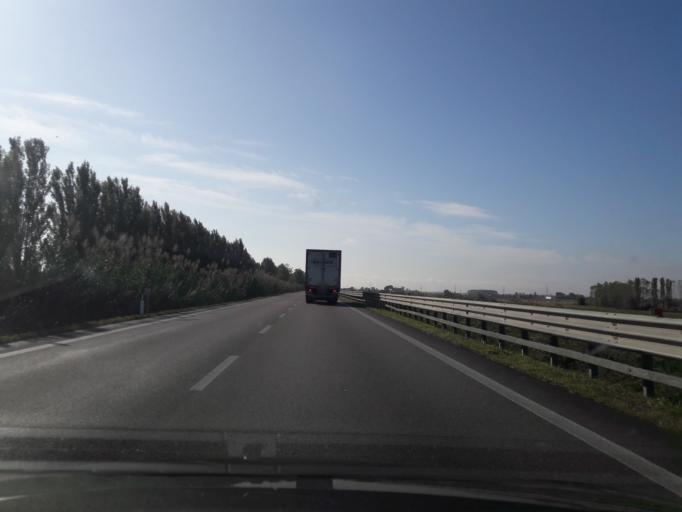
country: IT
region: Veneto
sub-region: Provincia di Padova
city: Codevigo
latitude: 45.3093
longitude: 12.1317
